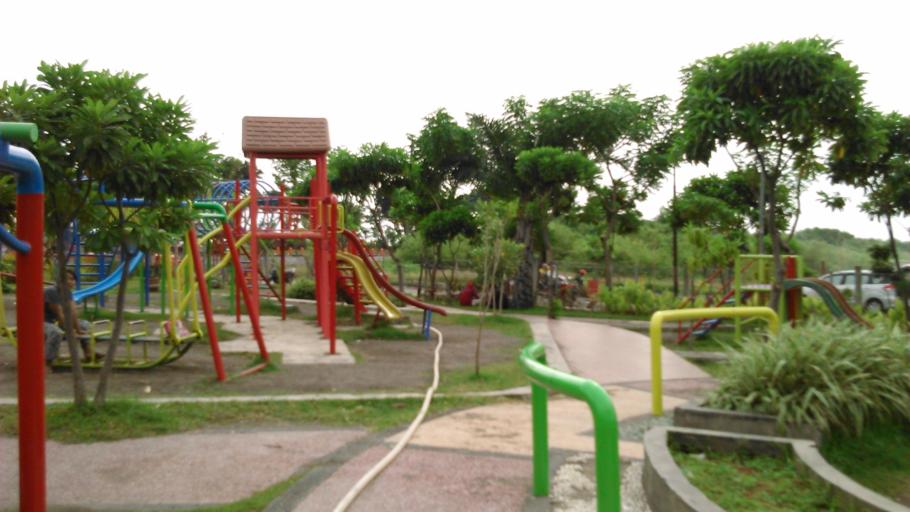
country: ID
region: East Java
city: Labansari
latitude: -7.2262
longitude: 112.7872
